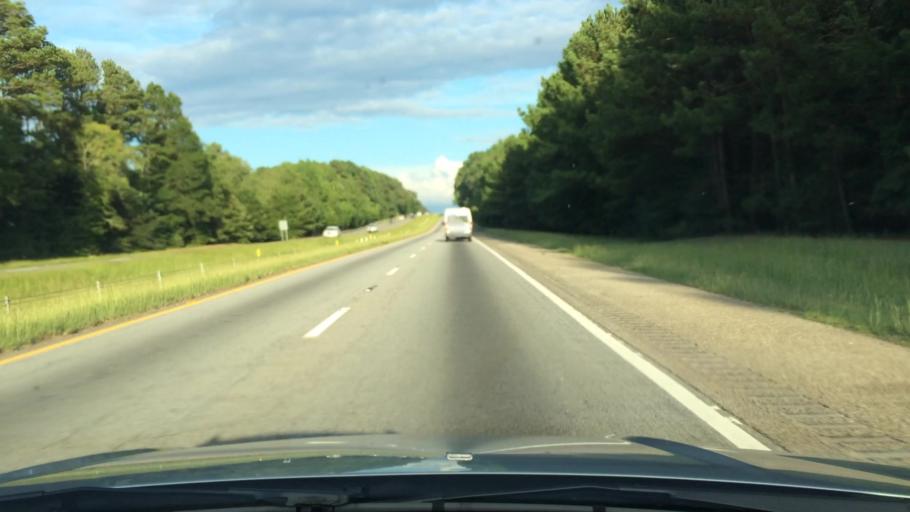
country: US
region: South Carolina
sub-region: Richland County
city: Lake Murray of Richland
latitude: 34.1631
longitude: -81.2825
